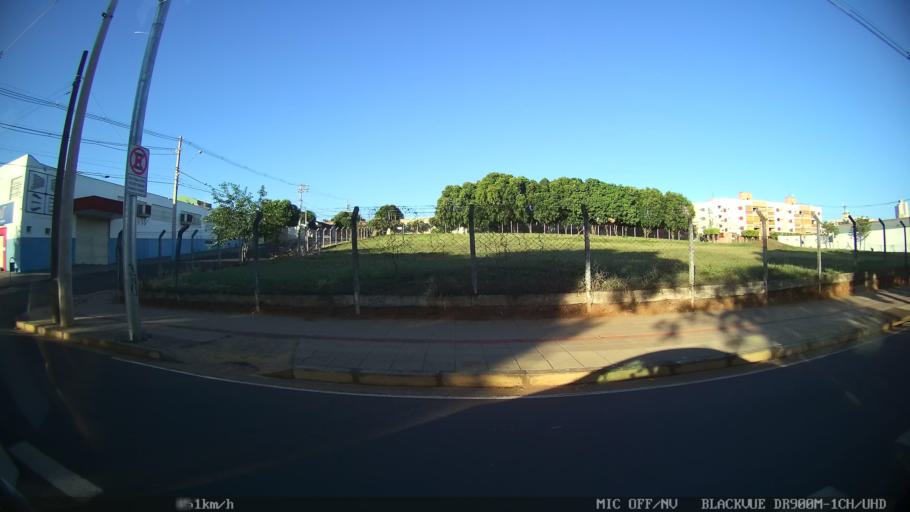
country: BR
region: Sao Paulo
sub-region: Sao Jose Do Rio Preto
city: Sao Jose do Rio Preto
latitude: -20.7918
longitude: -49.3761
